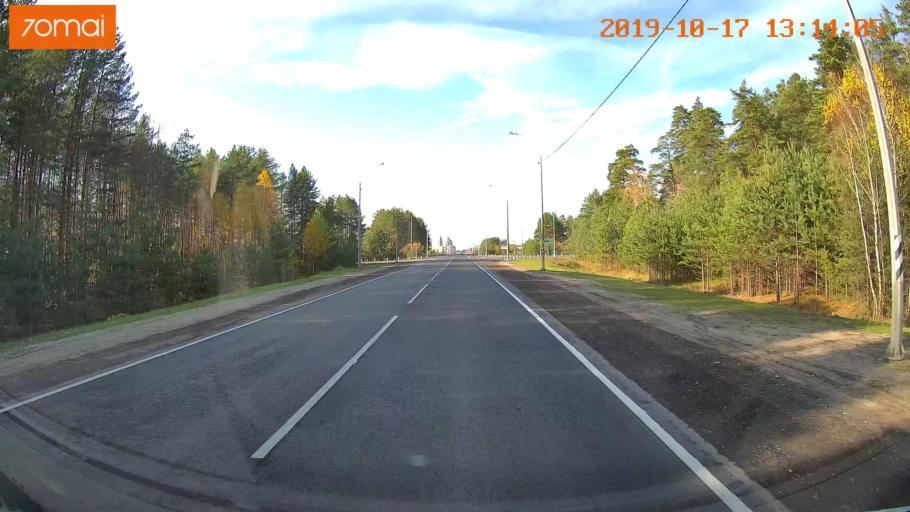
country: RU
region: Rjazan
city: Gus'-Zheleznyy
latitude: 55.0501
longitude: 41.1777
